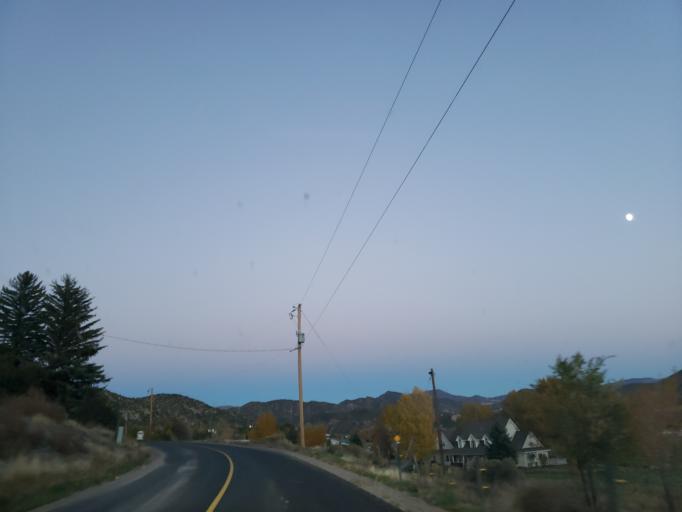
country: US
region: Colorado
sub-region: Garfield County
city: New Castle
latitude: 39.5586
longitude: -107.5794
